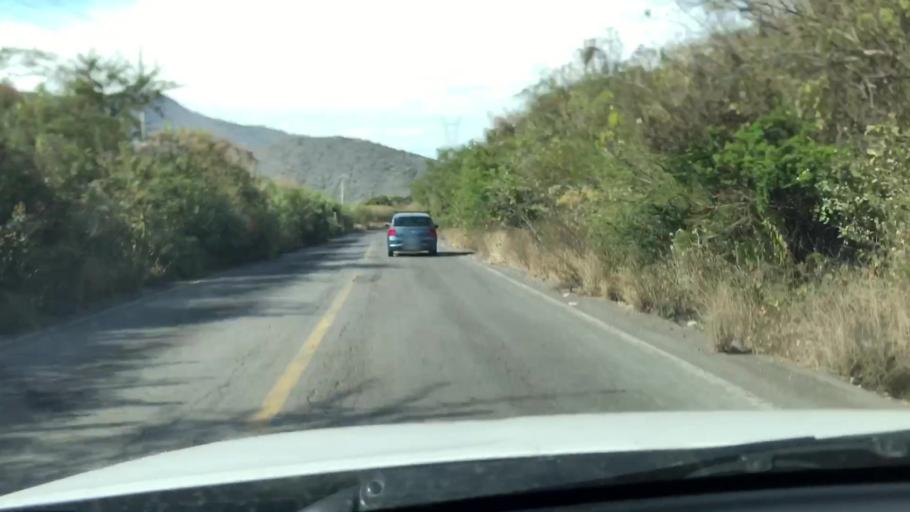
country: MX
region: Jalisco
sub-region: Zacoalco de Torres
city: Barranca de Otates (Barranca de Otatan)
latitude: 20.2325
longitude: -103.6846
